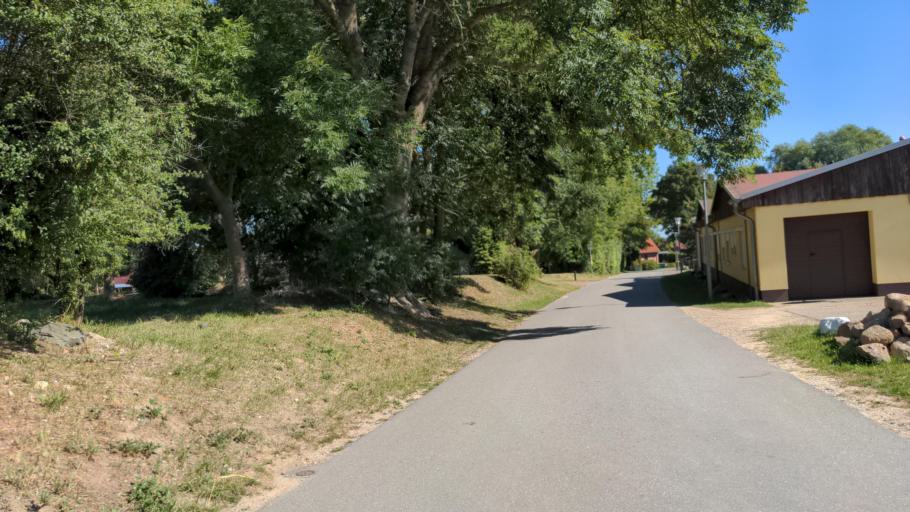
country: DE
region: Mecklenburg-Vorpommern
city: Klutz
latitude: 53.9879
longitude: 11.1743
